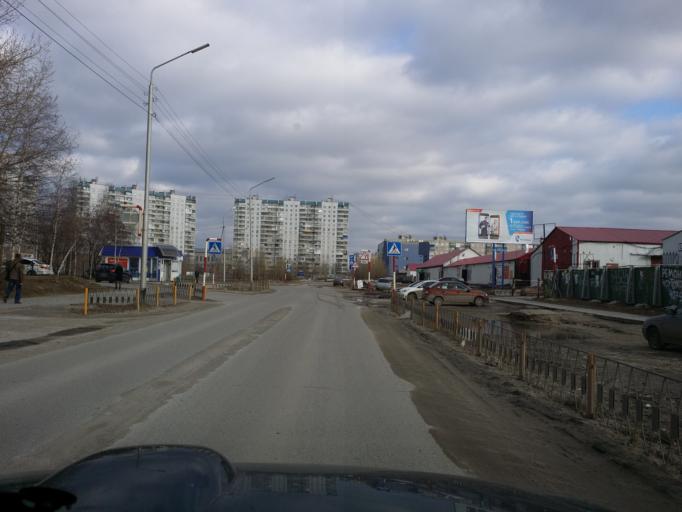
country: RU
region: Khanty-Mansiyskiy Avtonomnyy Okrug
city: Nizhnevartovsk
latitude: 60.9392
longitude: 76.6023
